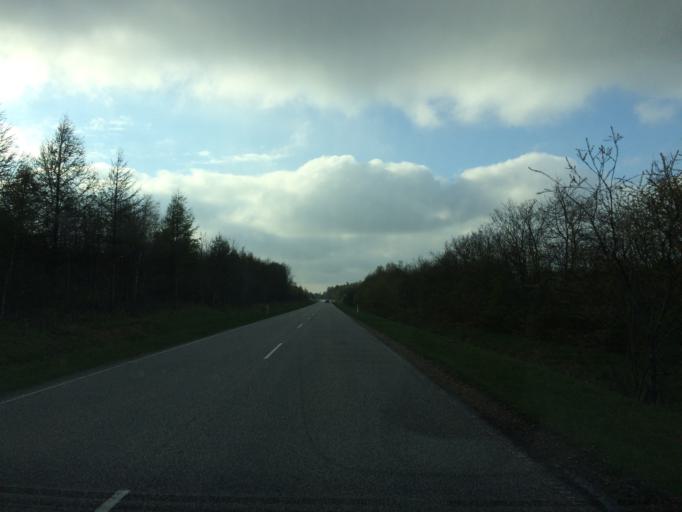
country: DK
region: Central Jutland
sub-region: Viborg Kommune
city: Karup
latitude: 56.3325
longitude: 9.0983
